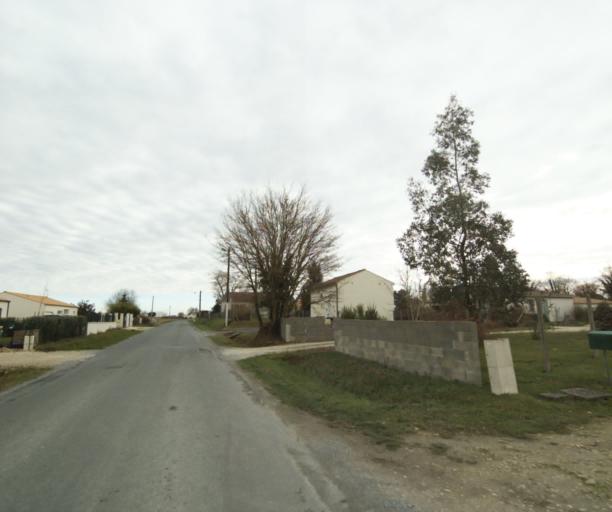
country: FR
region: Poitou-Charentes
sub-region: Departement de la Charente-Maritime
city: Corme-Royal
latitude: 45.7440
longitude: -0.8072
